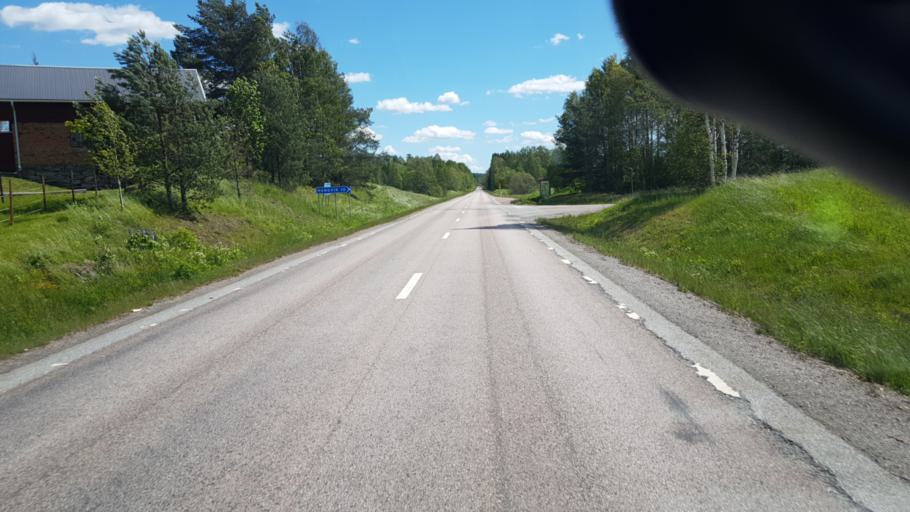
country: SE
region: Vaermland
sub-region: Arvika Kommun
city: Arvika
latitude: 59.6361
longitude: 12.7961
